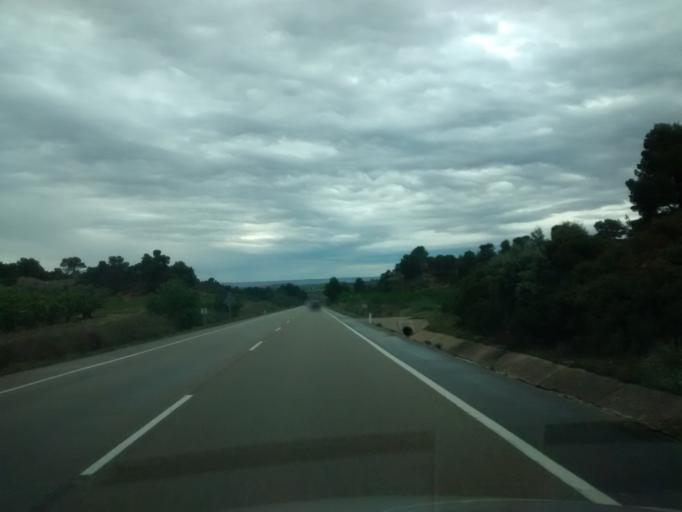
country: ES
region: Aragon
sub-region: Provincia de Zaragoza
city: Maella
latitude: 41.1644
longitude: 0.0782
